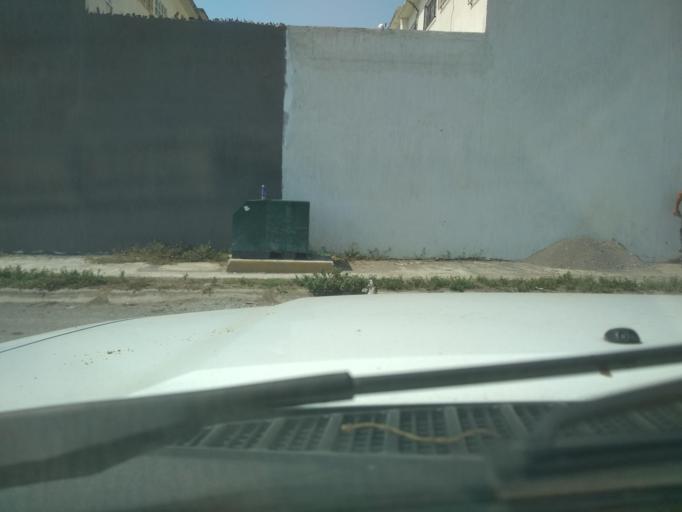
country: MX
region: Veracruz
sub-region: Veracruz
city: Lomas de Rio Medio Cuatro
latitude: 19.1930
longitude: -96.2083
